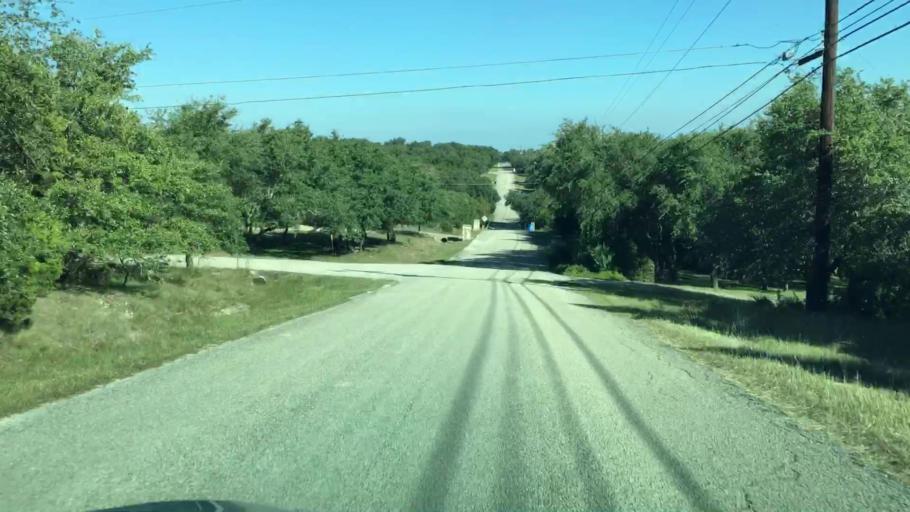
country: US
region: Texas
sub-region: Hays County
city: Dripping Springs
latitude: 30.1916
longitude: -98.0191
